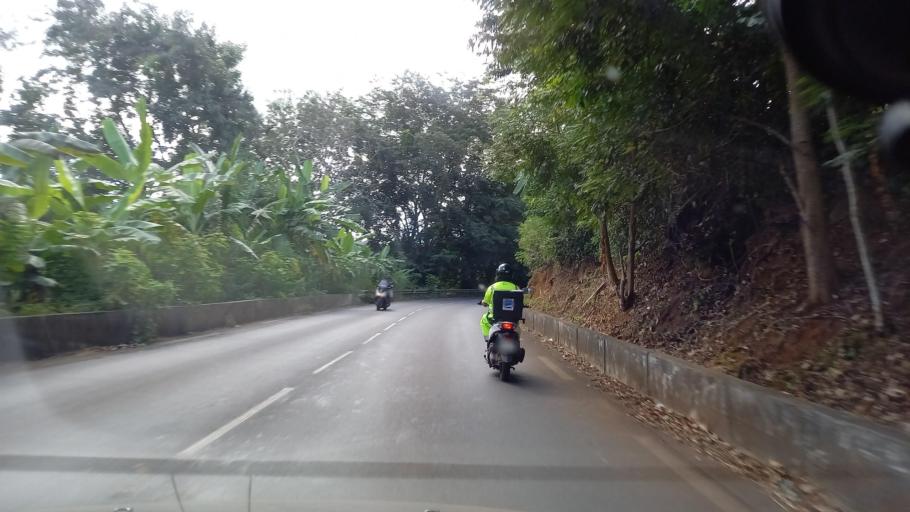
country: YT
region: Ouangani
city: Ouangani
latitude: -12.8358
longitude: 45.1528
